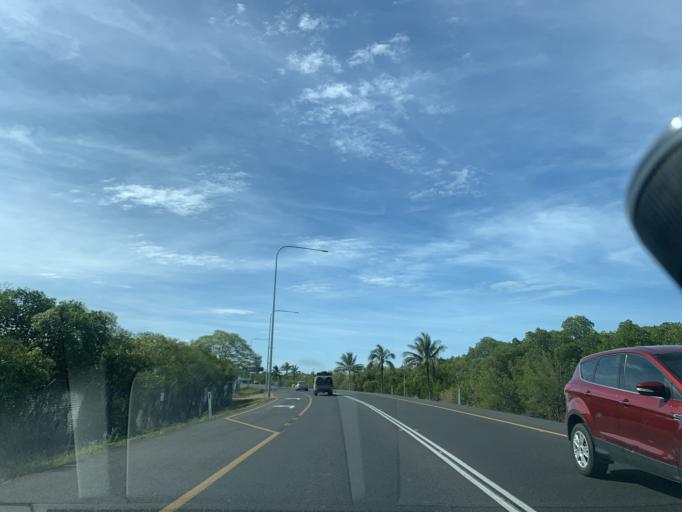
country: AU
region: Queensland
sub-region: Cairns
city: Cairns
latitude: -16.8817
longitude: 145.7601
